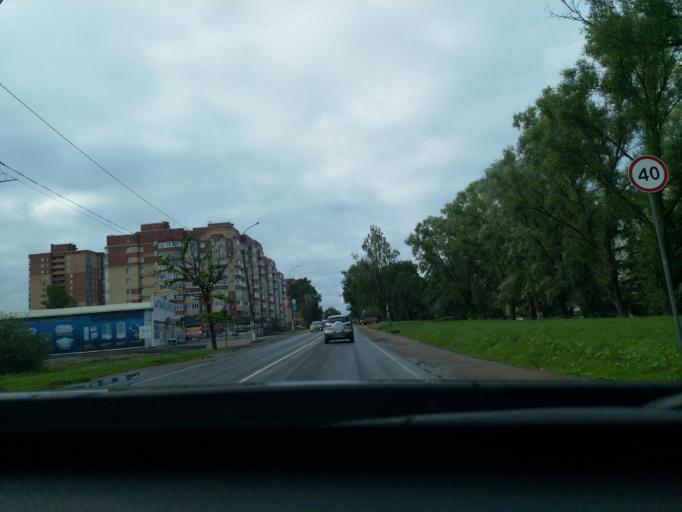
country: RU
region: Leningrad
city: Nikol'skoye
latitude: 59.6970
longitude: 30.7848
